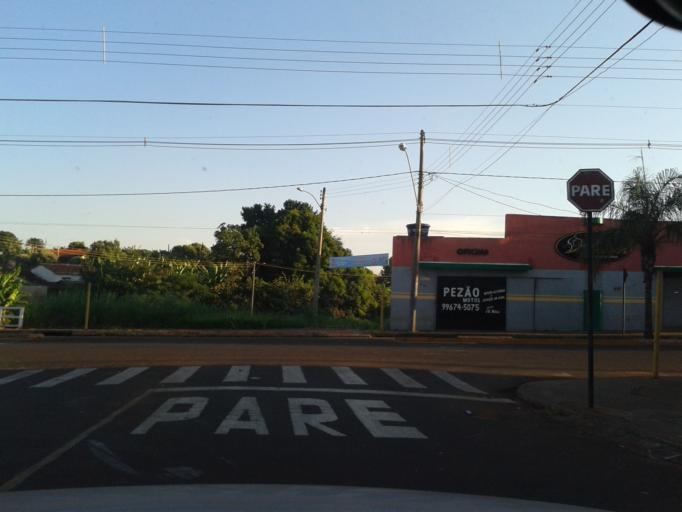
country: BR
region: Minas Gerais
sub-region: Ituiutaba
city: Ituiutaba
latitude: -18.9765
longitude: -49.4693
